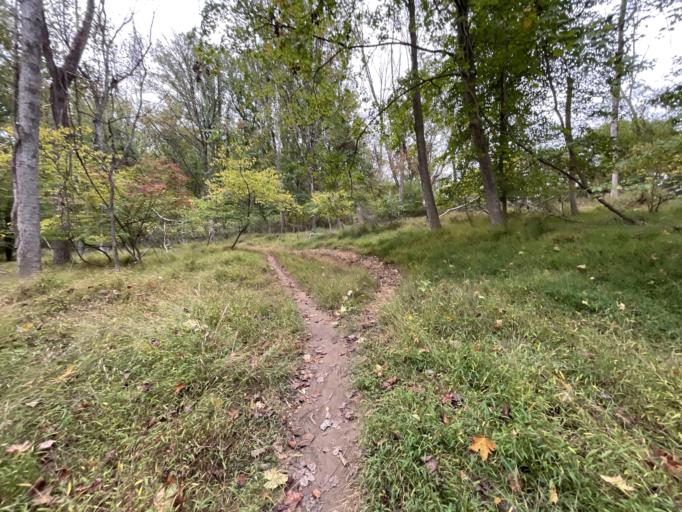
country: US
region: Maryland
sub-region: Baltimore County
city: Hampton
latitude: 39.4278
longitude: -76.5750
